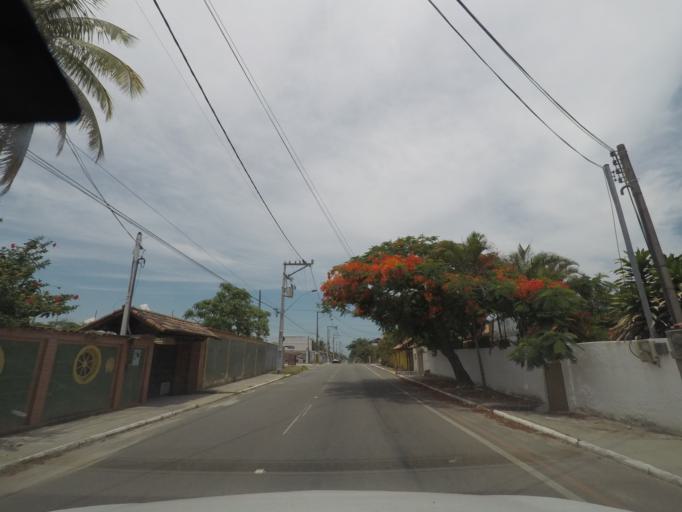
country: BR
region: Rio de Janeiro
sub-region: Marica
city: Marica
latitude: -22.9686
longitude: -42.9554
